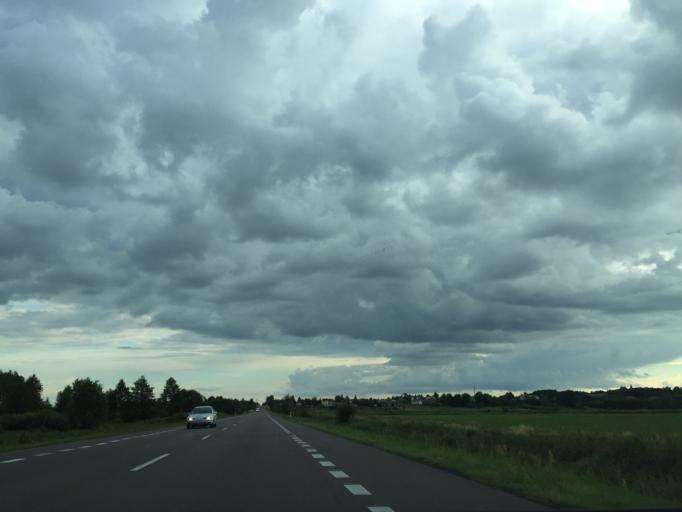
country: PL
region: Lublin Voivodeship
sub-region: Powiat radzynski
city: Borki
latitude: 51.7258
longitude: 22.5361
